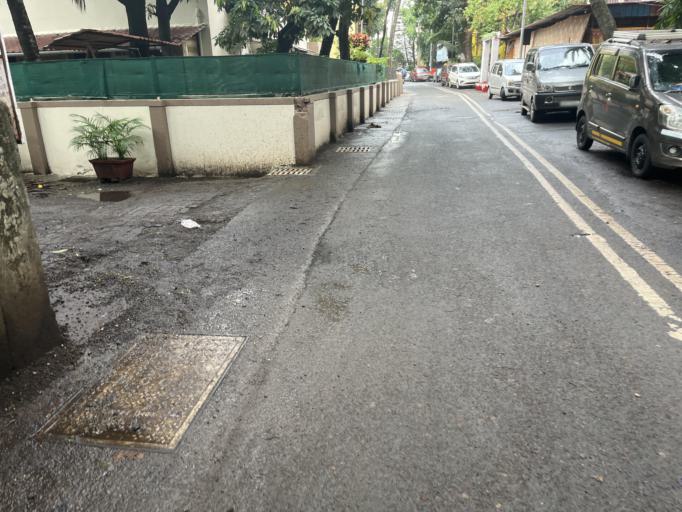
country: IN
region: Maharashtra
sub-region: Mumbai Suburban
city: Borivli
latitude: 19.2360
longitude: 72.8657
